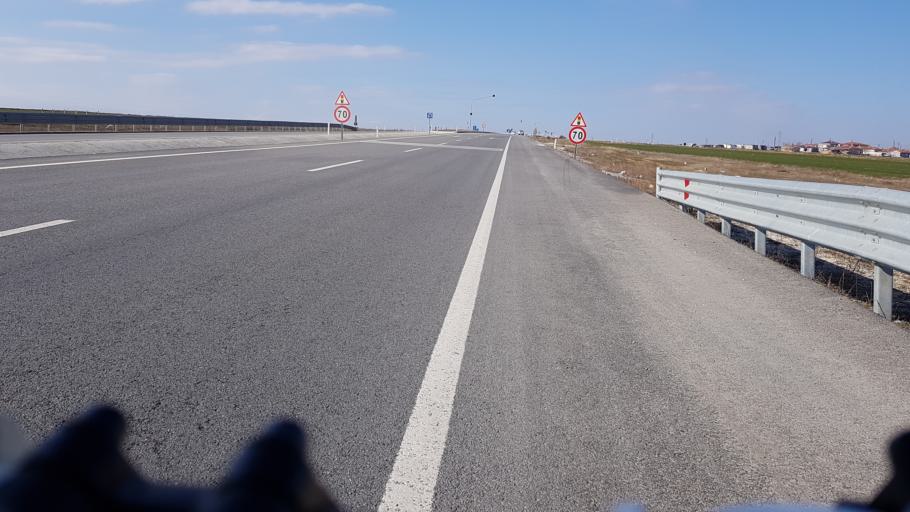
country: TR
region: Tekirdag
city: Saray
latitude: 41.4282
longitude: 27.9112
